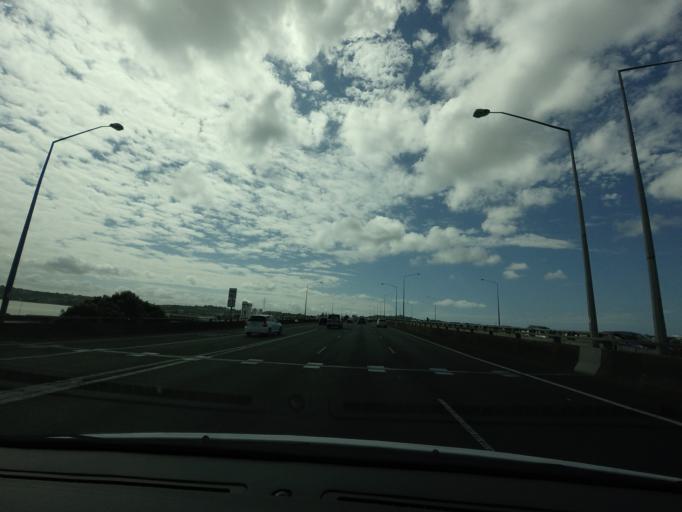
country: NZ
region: Auckland
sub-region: Auckland
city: Mangere
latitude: -36.9364
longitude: 174.7894
